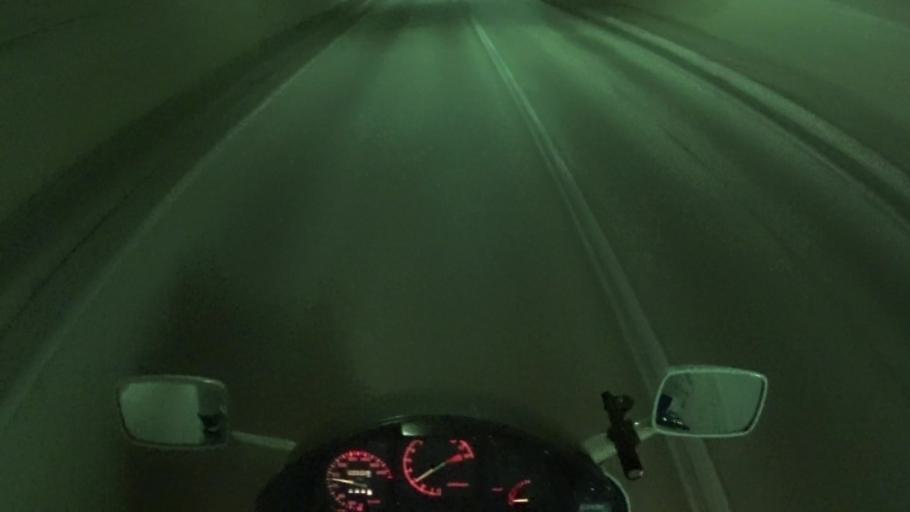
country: JP
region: Kyoto
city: Miyazu
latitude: 35.7291
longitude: 135.0939
